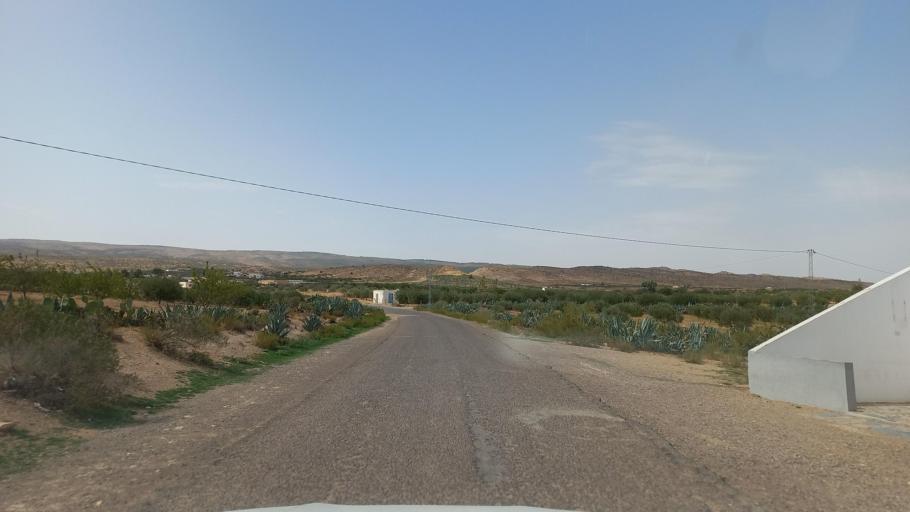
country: TN
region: Al Qasrayn
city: Kasserine
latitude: 35.2980
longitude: 8.9561
